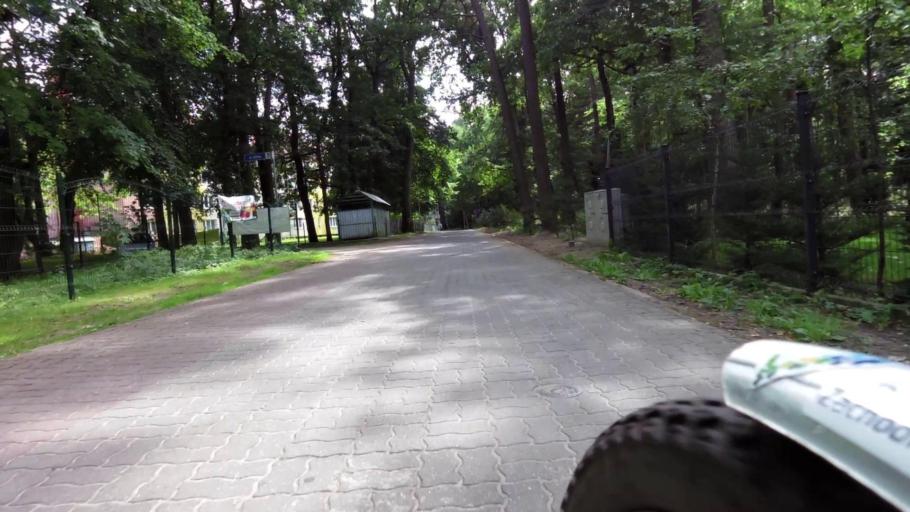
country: PL
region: West Pomeranian Voivodeship
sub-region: Powiat kolobrzeski
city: Ustronie Morskie
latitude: 54.2181
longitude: 15.7708
